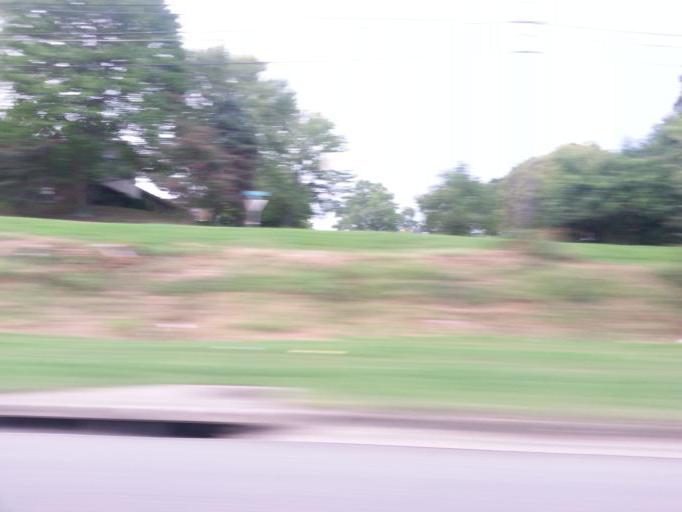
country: US
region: Alabama
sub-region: Madison County
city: Huntsville
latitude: 34.7349
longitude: -86.6310
